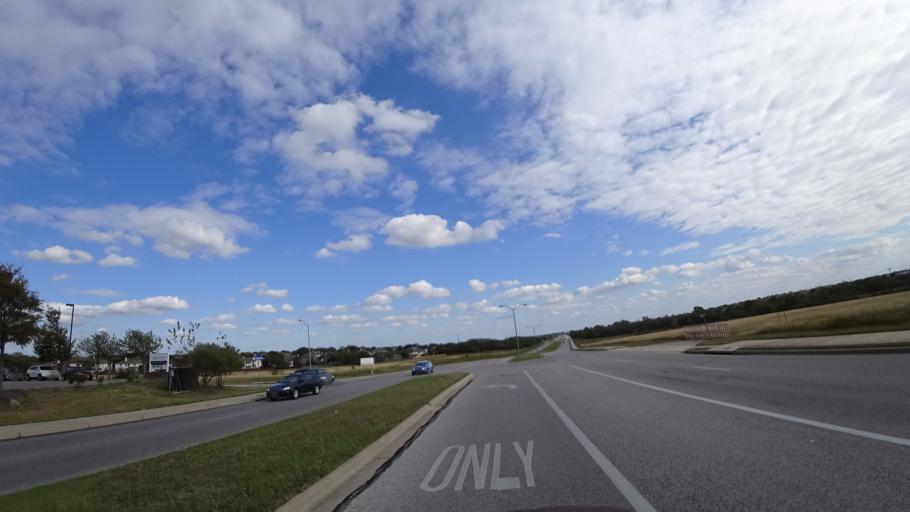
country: US
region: Texas
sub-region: Travis County
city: Pflugerville
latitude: 30.4290
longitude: -97.6352
